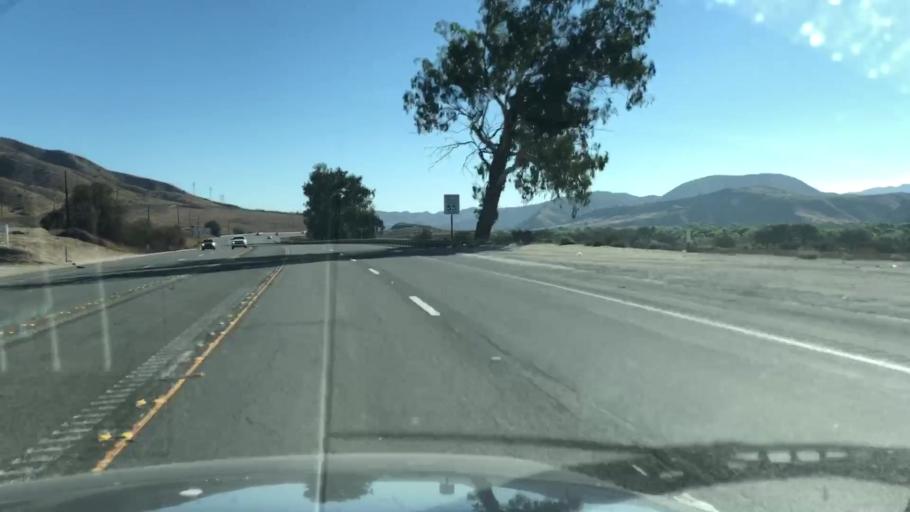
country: US
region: California
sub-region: Los Angeles County
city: Val Verde
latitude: 34.4066
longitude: -118.6880
